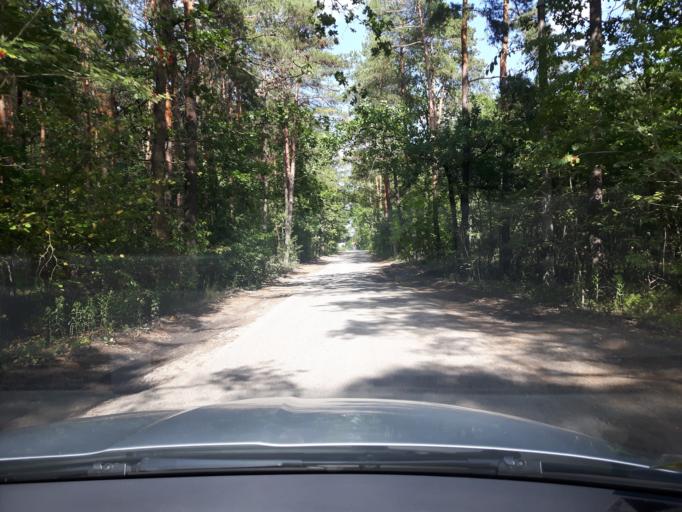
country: PL
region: Masovian Voivodeship
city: Zielonka
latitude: 52.2901
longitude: 21.1482
